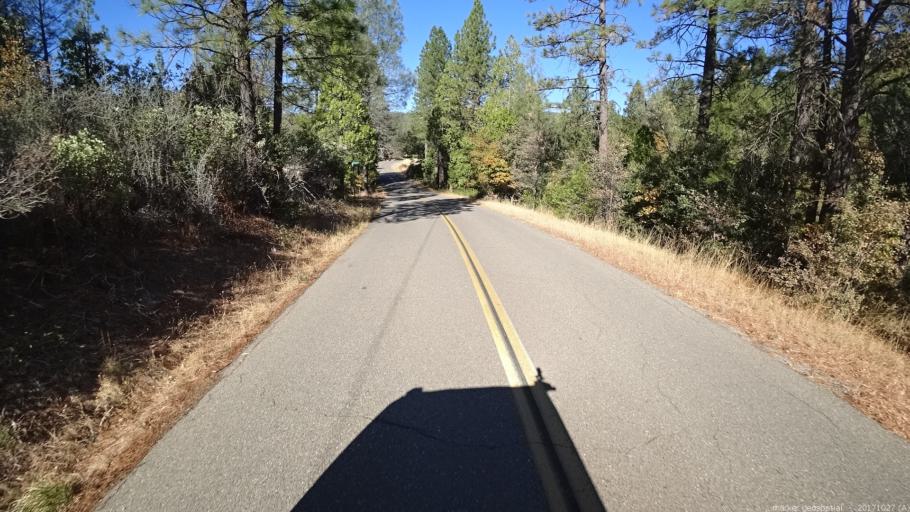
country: US
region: California
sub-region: Shasta County
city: Shingletown
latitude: 40.6694
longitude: -121.8833
